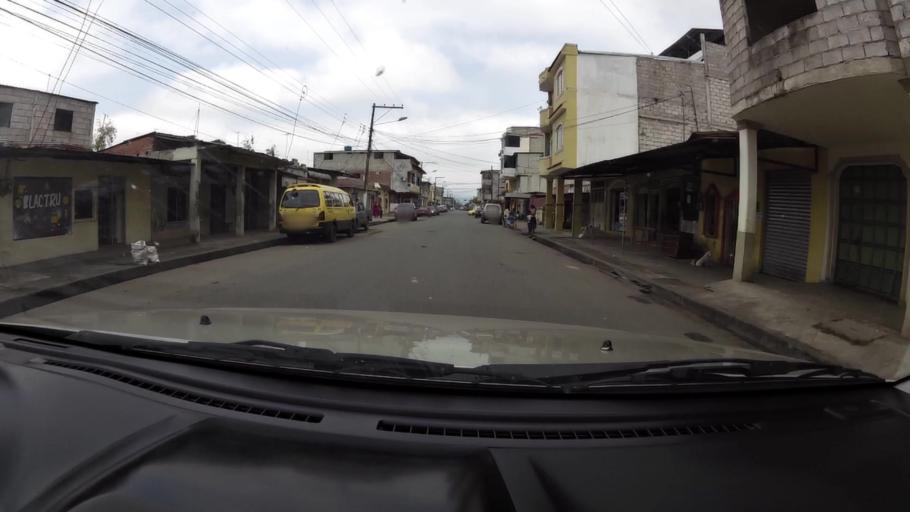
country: EC
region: El Oro
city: Pasaje
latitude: -3.2436
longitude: -79.8314
